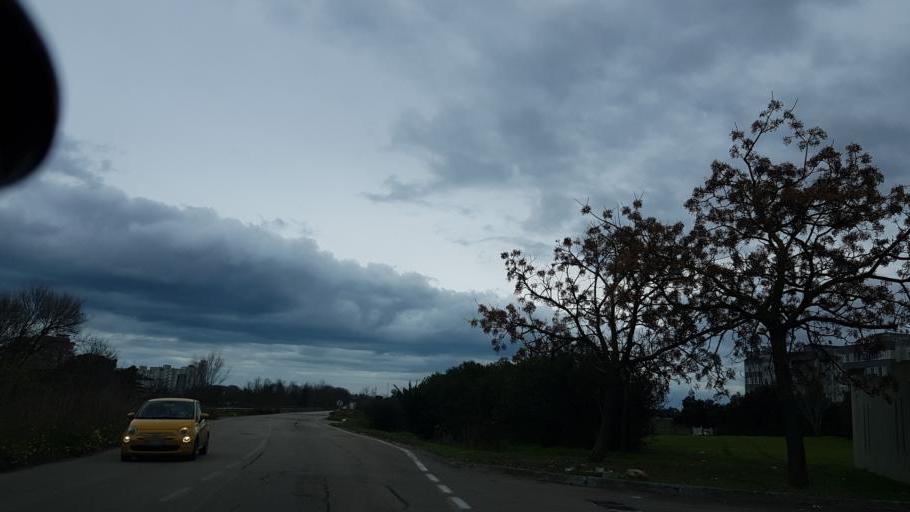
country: IT
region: Apulia
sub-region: Provincia di Brindisi
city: Brindisi
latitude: 40.6196
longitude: 17.9347
